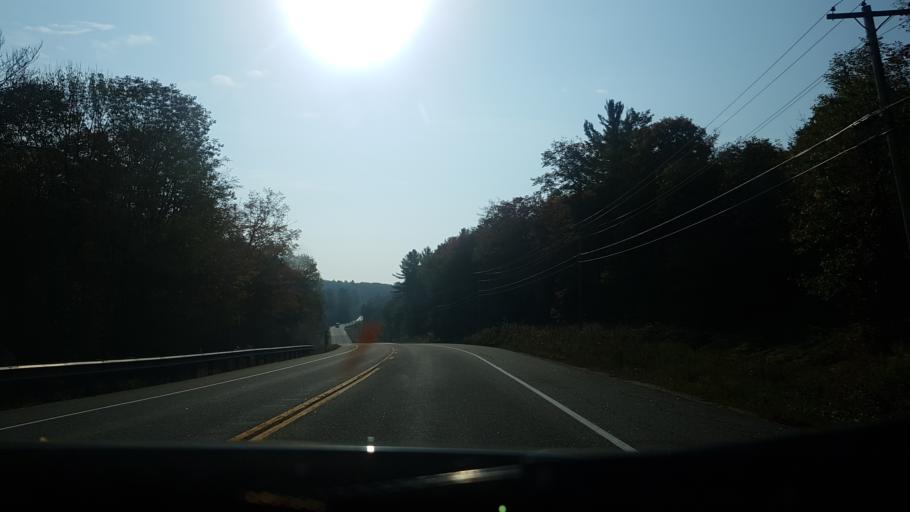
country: CA
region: Ontario
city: Bracebridge
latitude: 45.2422
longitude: -79.5909
